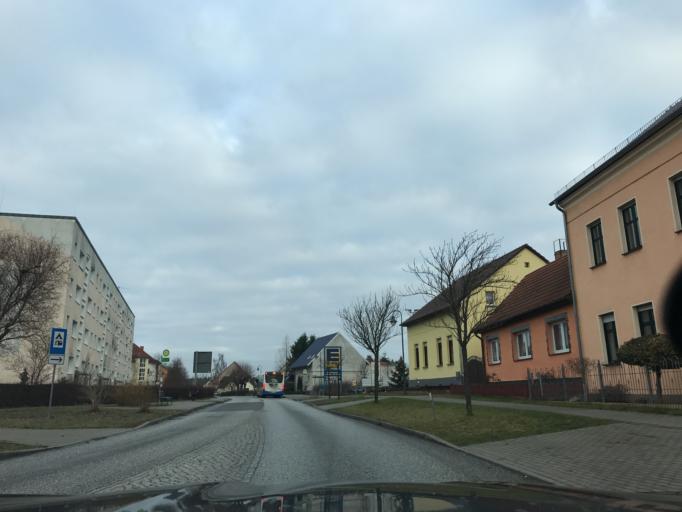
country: DE
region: Brandenburg
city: Gross Kreutz
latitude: 52.3189
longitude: 12.7372
